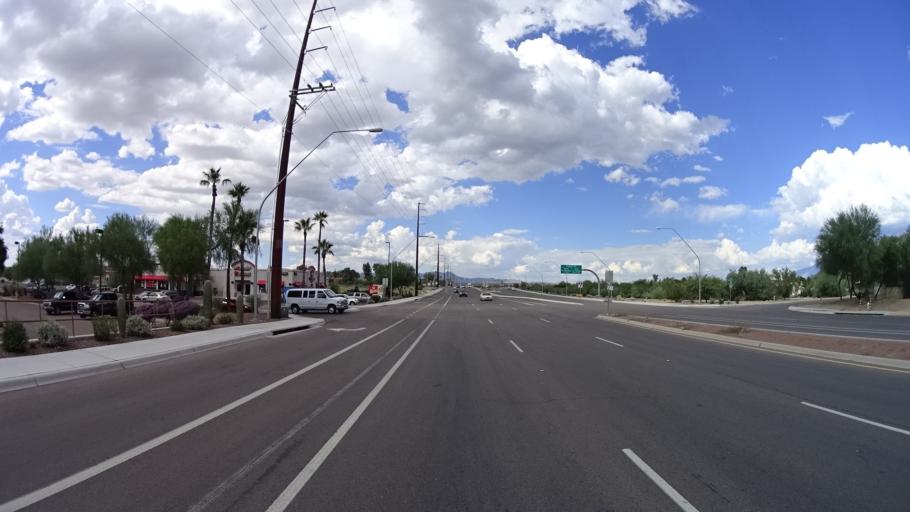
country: US
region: Arizona
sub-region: Pima County
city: Casas Adobes
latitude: 32.3450
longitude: -111.0129
